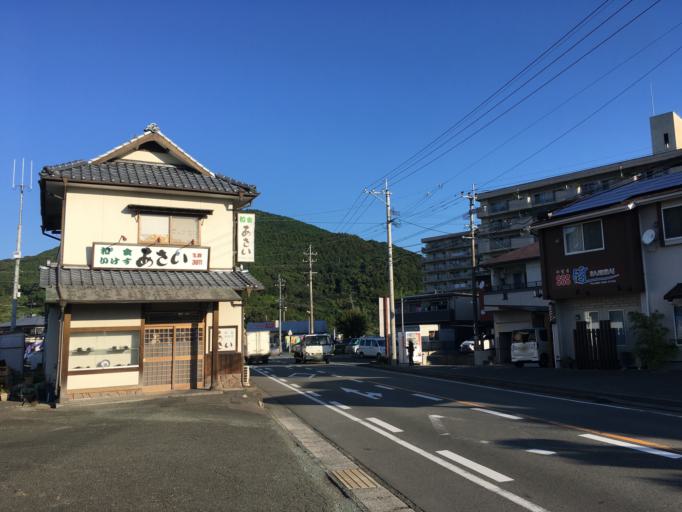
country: JP
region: Kumamoto
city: Kumamoto
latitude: 32.7862
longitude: 130.6633
